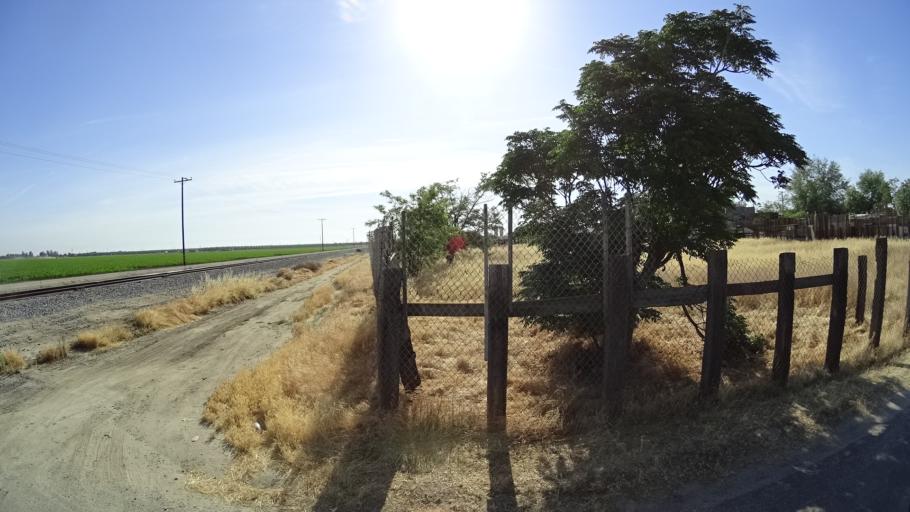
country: US
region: California
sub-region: Kings County
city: Hanford
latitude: 36.3305
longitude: -119.6094
